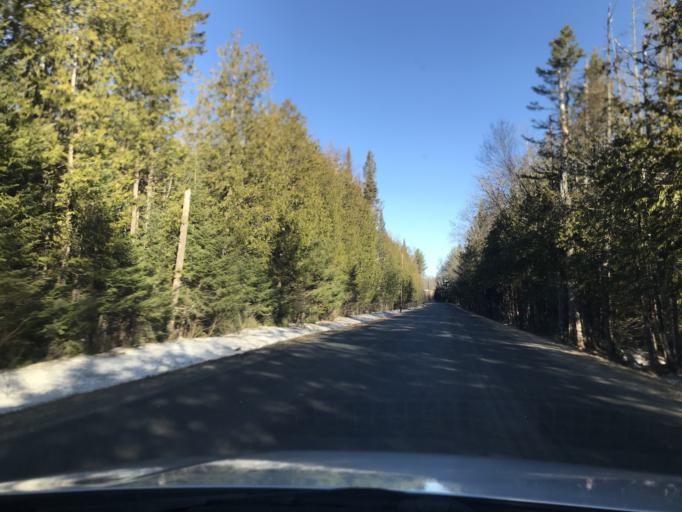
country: US
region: Wisconsin
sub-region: Marinette County
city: Niagara
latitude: 45.3774
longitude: -88.0236
